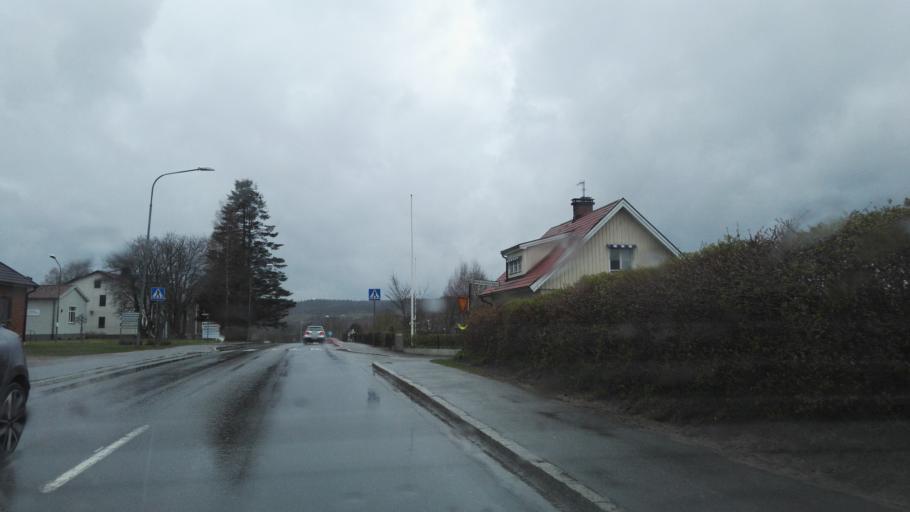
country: SE
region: Skane
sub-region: Kristianstads Kommun
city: Degeberga
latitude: 55.7266
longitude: 14.0988
